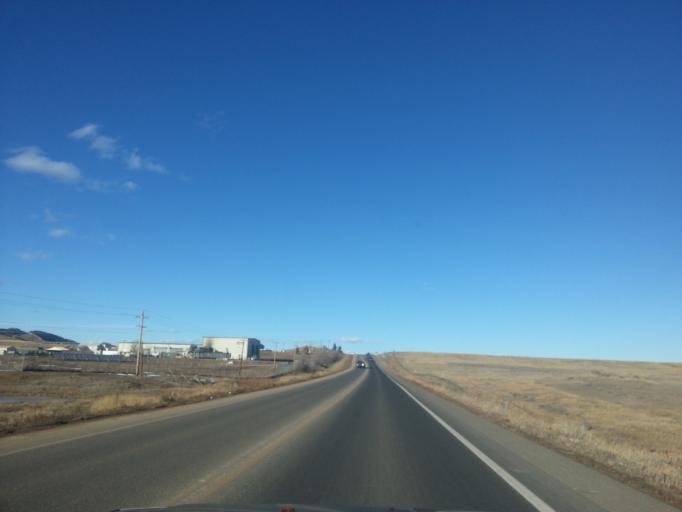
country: US
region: Colorado
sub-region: Larimer County
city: Fort Collins
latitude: 40.5008
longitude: -105.1153
